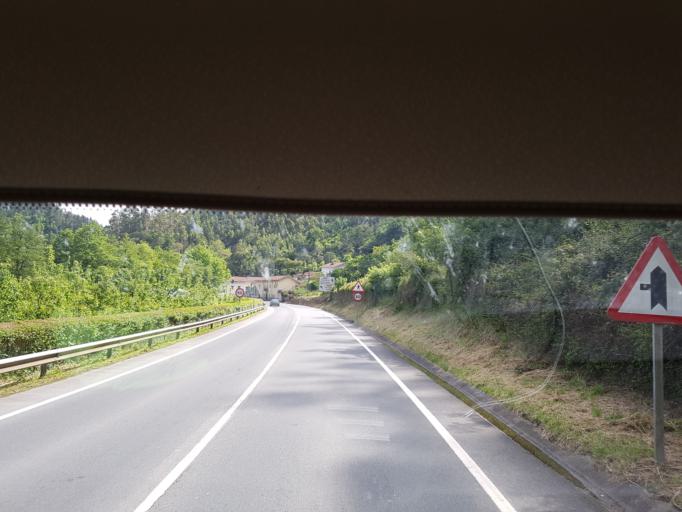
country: ES
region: Basque Country
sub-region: Bizkaia
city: Sopuerta
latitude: 43.2825
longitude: -3.1393
